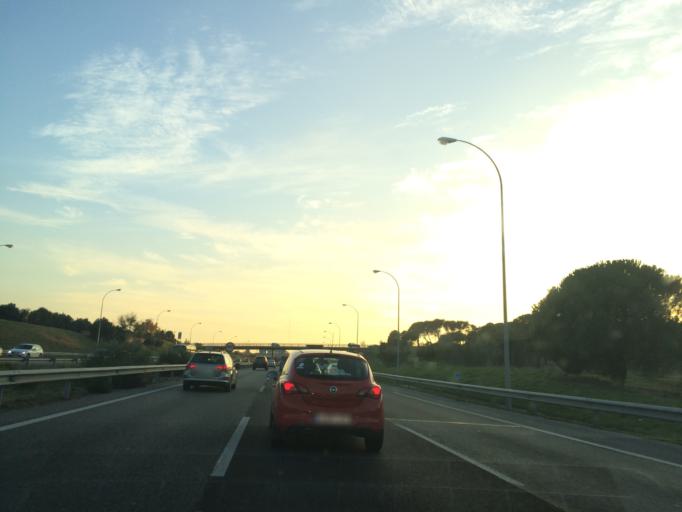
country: ES
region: Madrid
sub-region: Provincia de Madrid
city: Pozuelo de Alarcon
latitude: 40.4551
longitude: -3.8163
